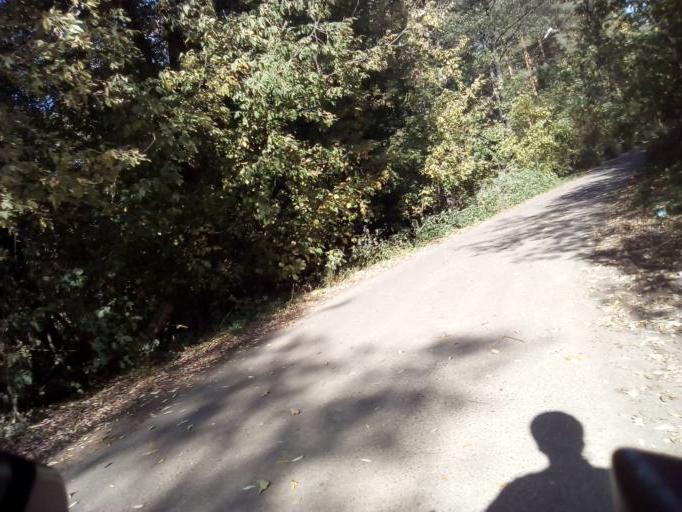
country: RU
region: Moskovskaya
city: Ramenskoye
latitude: 55.5472
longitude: 38.3014
